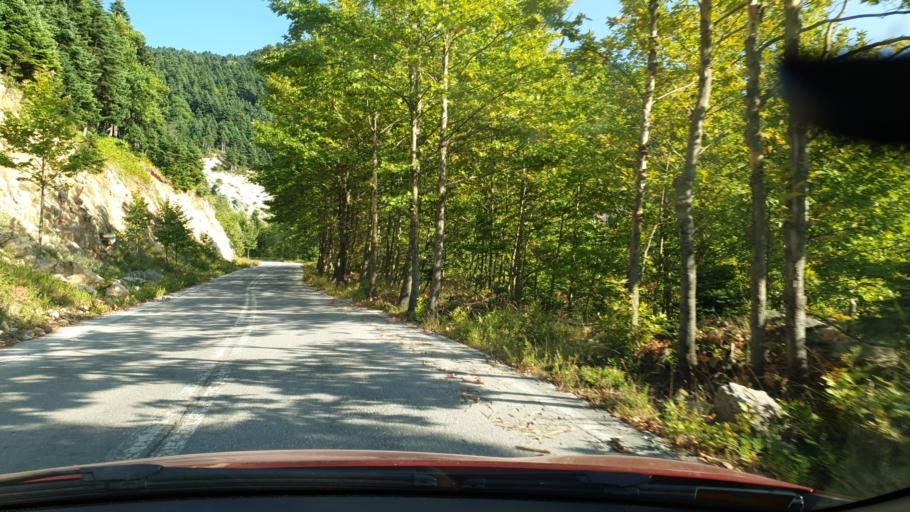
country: GR
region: Central Greece
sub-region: Nomos Evvoias
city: Yimnon
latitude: 38.6079
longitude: 23.9189
